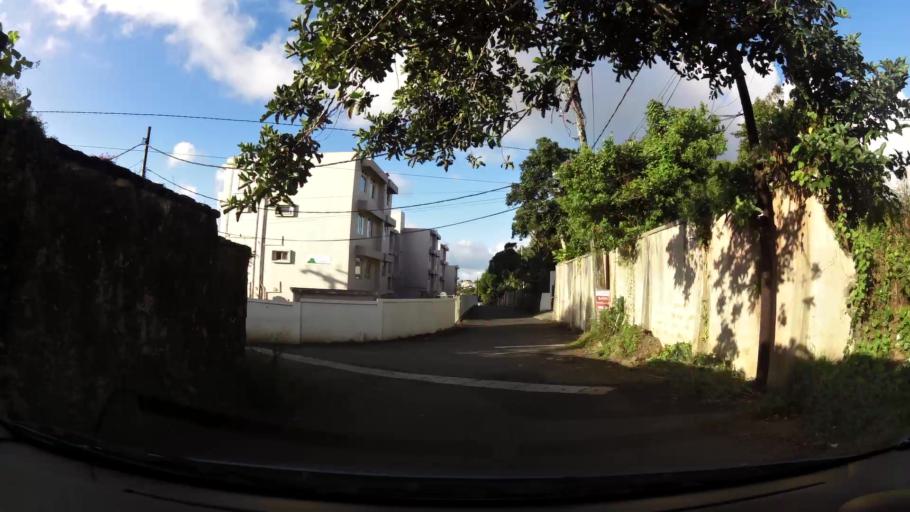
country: MU
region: Plaines Wilhems
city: Curepipe
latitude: -20.3146
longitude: 57.5162
